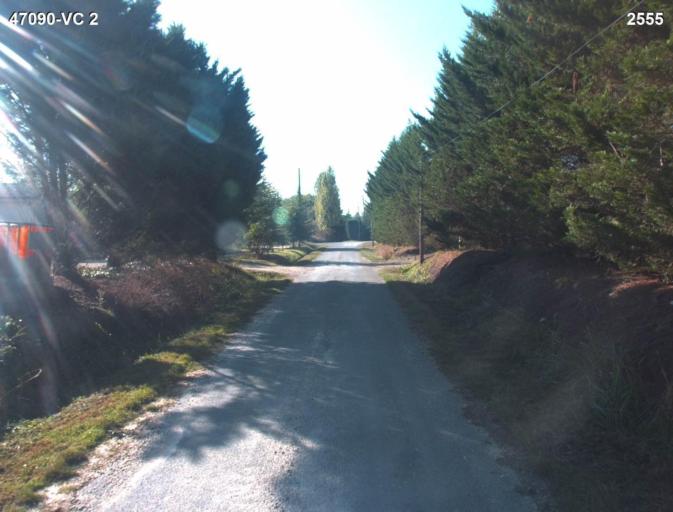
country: FR
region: Aquitaine
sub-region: Departement du Lot-et-Garonne
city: Nerac
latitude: 44.1723
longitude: 0.3758
